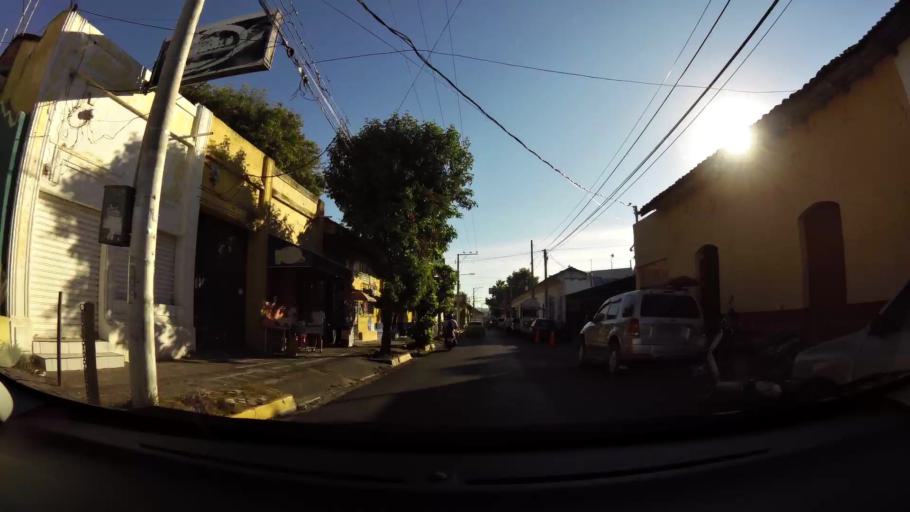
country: SV
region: San Miguel
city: San Miguel
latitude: 13.4838
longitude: -88.1787
